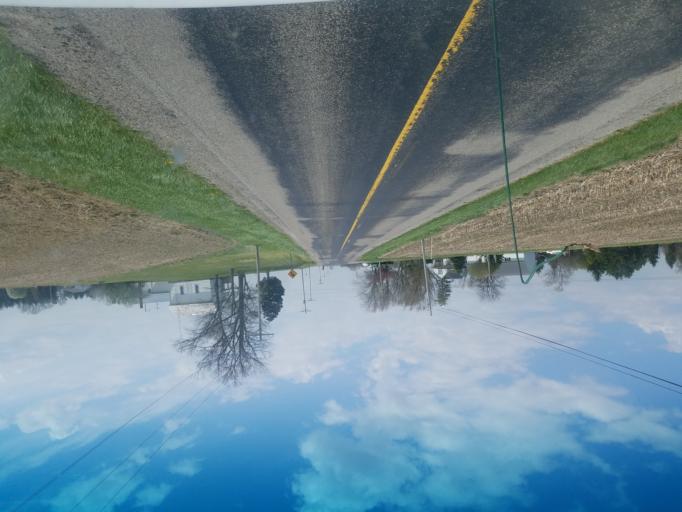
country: US
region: Ohio
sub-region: Hardin County
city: Kenton
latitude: 40.5878
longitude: -83.6766
